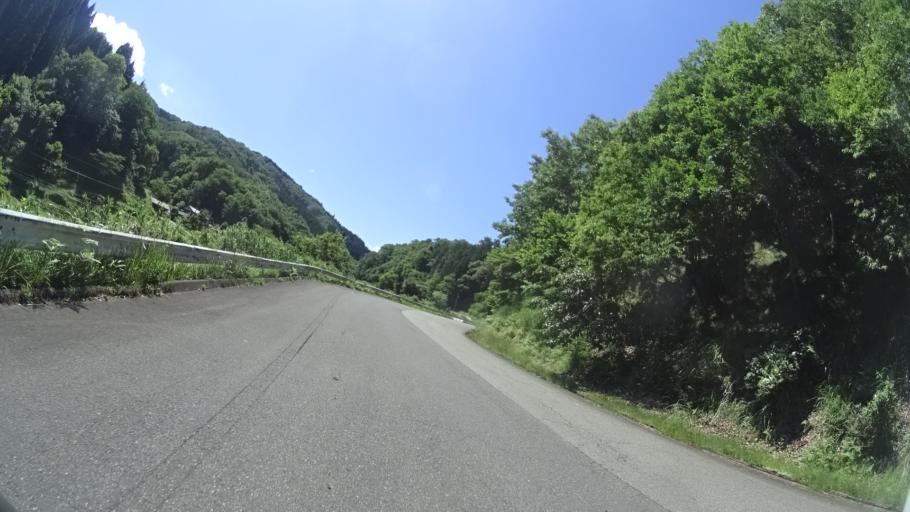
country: JP
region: Kyoto
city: Fukuchiyama
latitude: 35.4253
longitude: 135.0585
